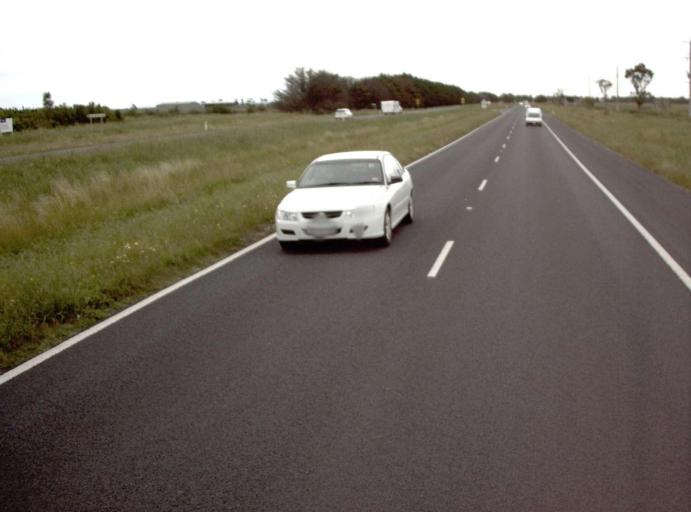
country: AU
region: Victoria
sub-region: Cardinia
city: Koo-Wee-Rup
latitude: -38.2399
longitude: 145.5241
